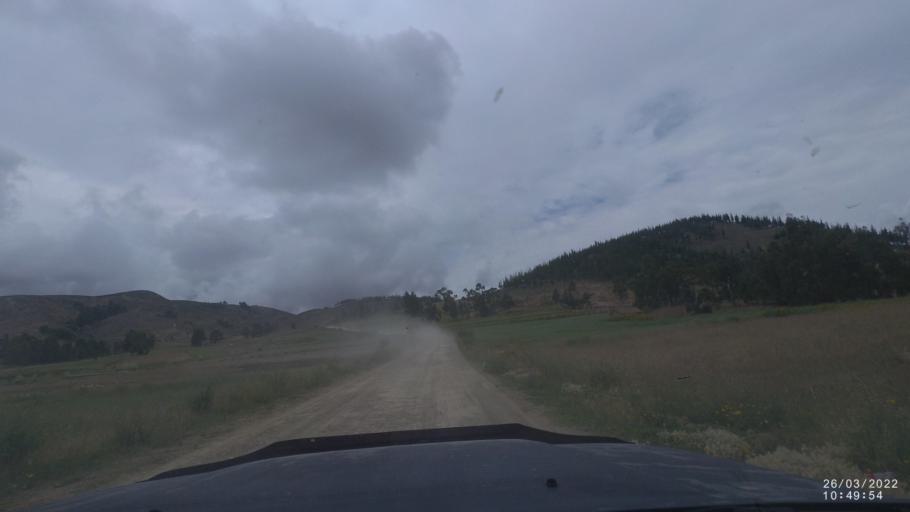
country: BO
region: Cochabamba
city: Tarata
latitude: -17.5047
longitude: -66.0338
